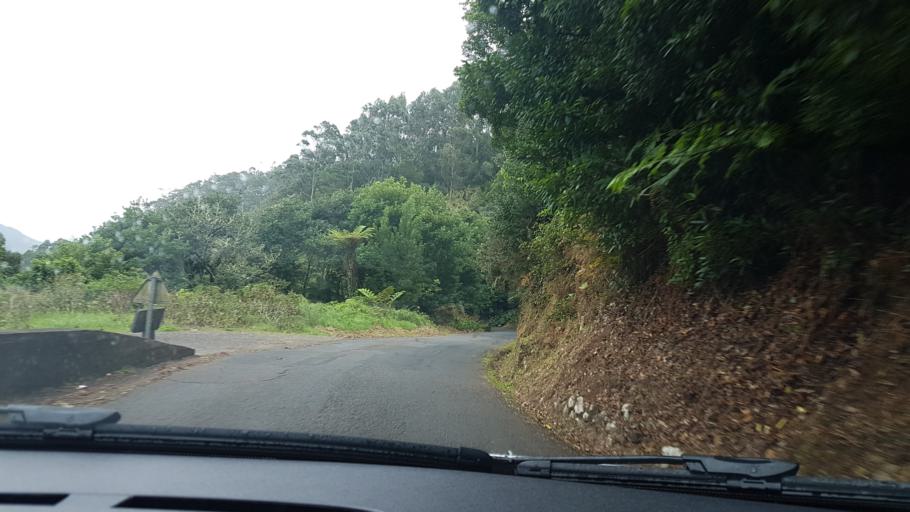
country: PT
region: Madeira
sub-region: Santa Cruz
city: Santa Cruz
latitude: 32.7277
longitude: -16.8152
